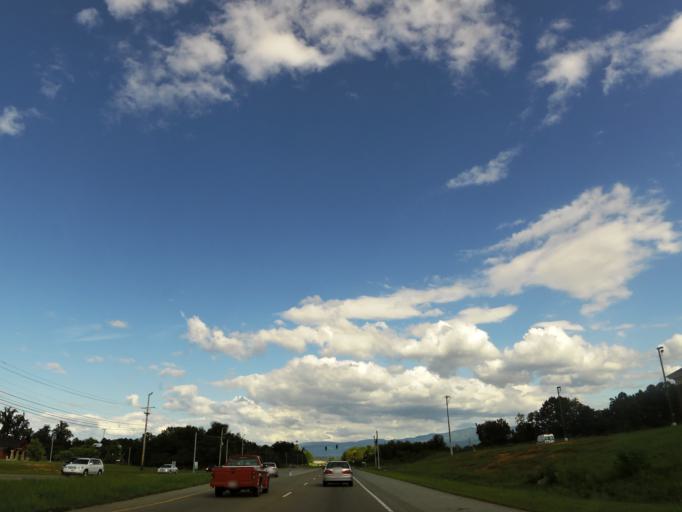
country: US
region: Tennessee
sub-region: Greene County
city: Tusculum
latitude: 36.1854
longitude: -82.7609
